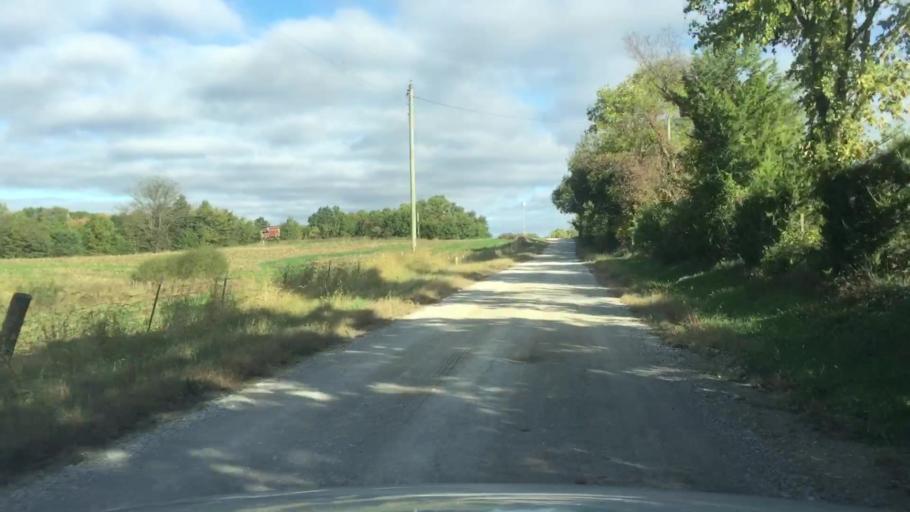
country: US
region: Missouri
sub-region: Howard County
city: New Franklin
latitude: 39.0879
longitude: -92.7828
